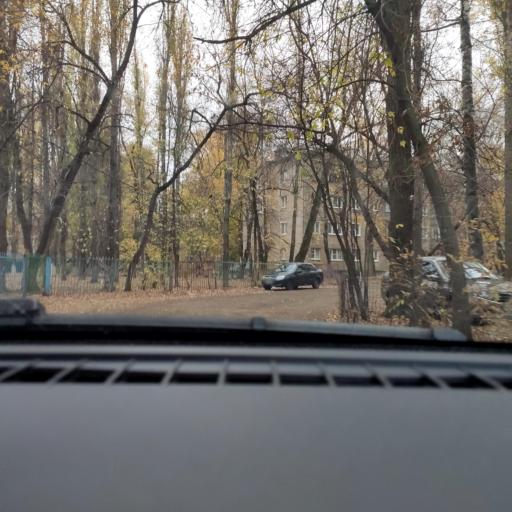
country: RU
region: Voronezj
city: Voronezh
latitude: 51.6829
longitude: 39.2577
